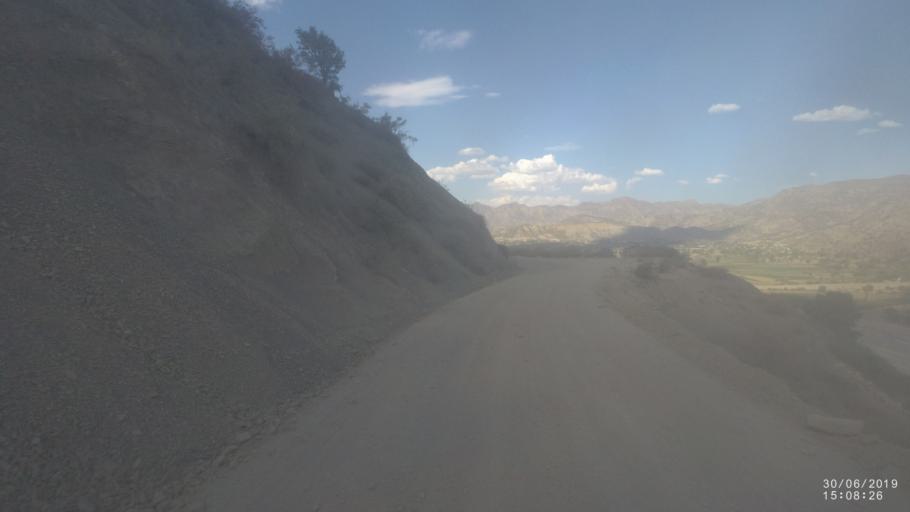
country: BO
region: Cochabamba
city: Irpa Irpa
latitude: -17.7315
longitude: -66.3022
